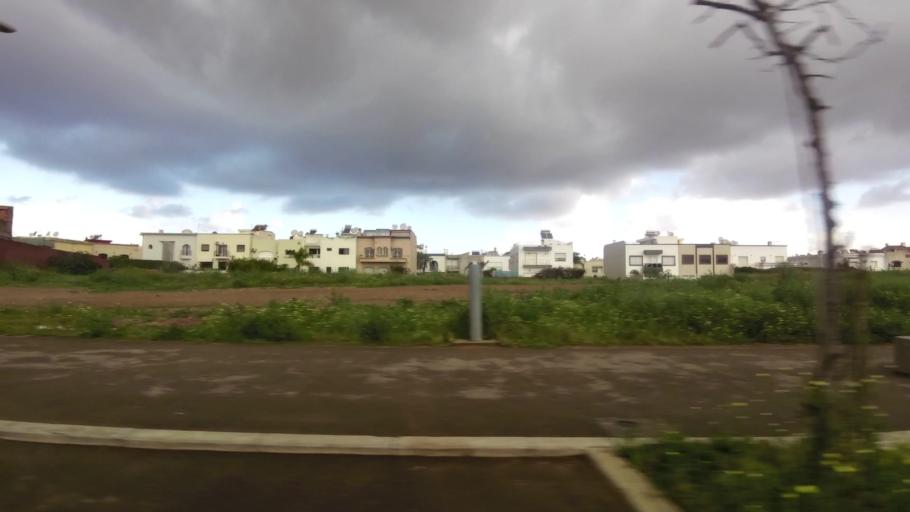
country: MA
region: Grand Casablanca
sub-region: Casablanca
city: Casablanca
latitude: 33.5455
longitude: -7.6587
